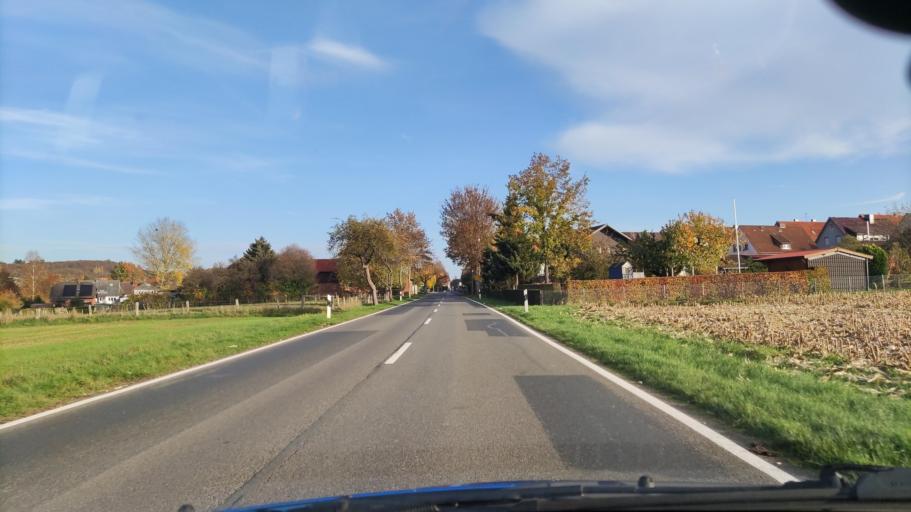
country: DE
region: Lower Saxony
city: Dassel
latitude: 51.7740
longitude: 9.7108
